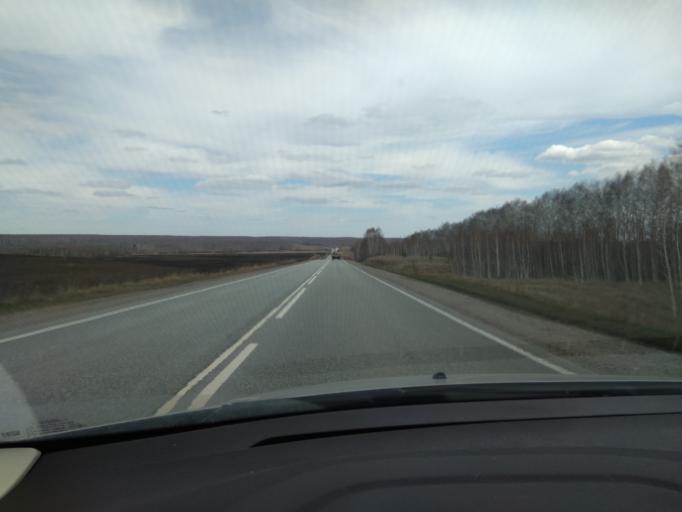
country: RU
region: Sverdlovsk
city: Yelanskiy
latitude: 56.7590
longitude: 62.3636
